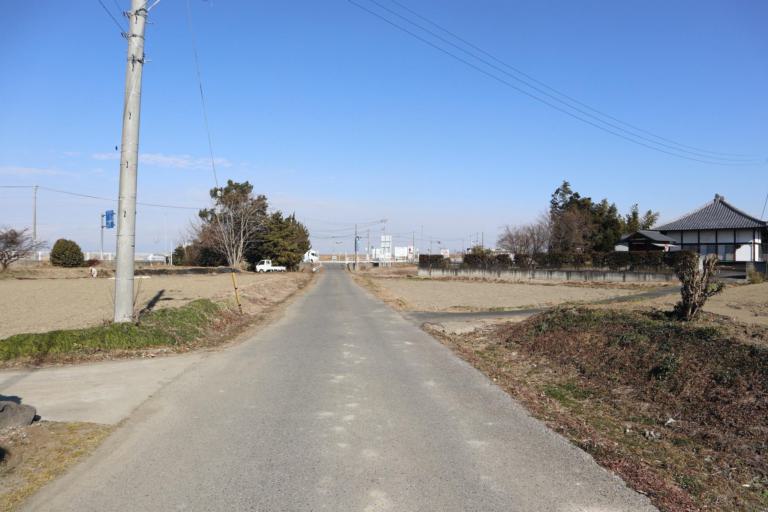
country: JP
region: Saitama
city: Fukiage-fujimi
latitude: 36.0799
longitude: 139.4304
